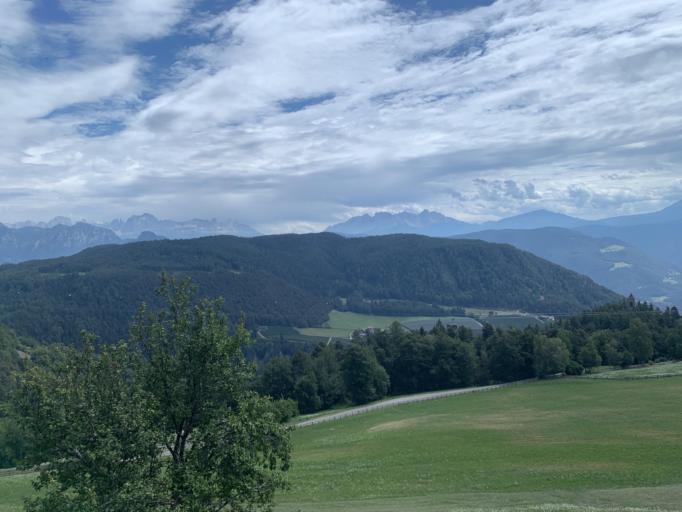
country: IT
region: Trentino-Alto Adige
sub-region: Bolzano
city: Soprabolzano
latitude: 46.5251
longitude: 11.3954
